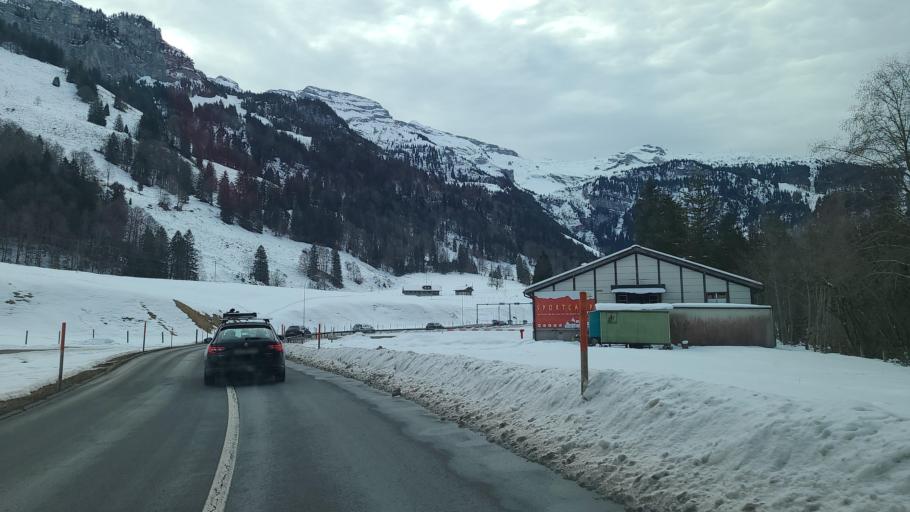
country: CH
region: Obwalden
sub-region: Obwalden
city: Sachseln
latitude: 46.8184
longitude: 8.2839
